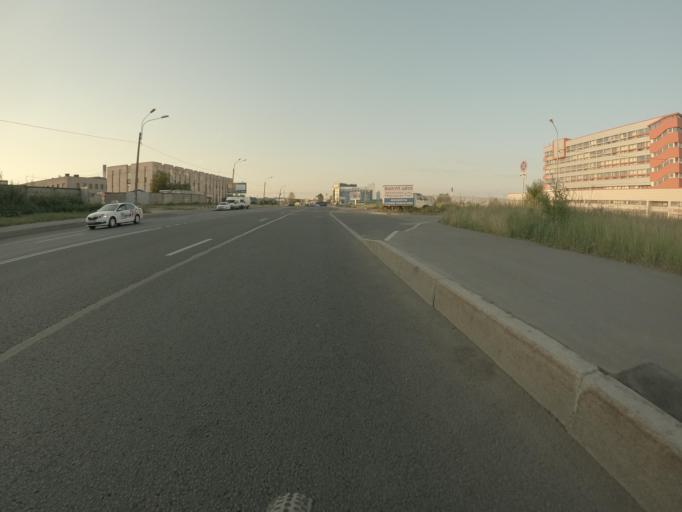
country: RU
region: St.-Petersburg
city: Avtovo
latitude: 59.8603
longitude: 30.2854
